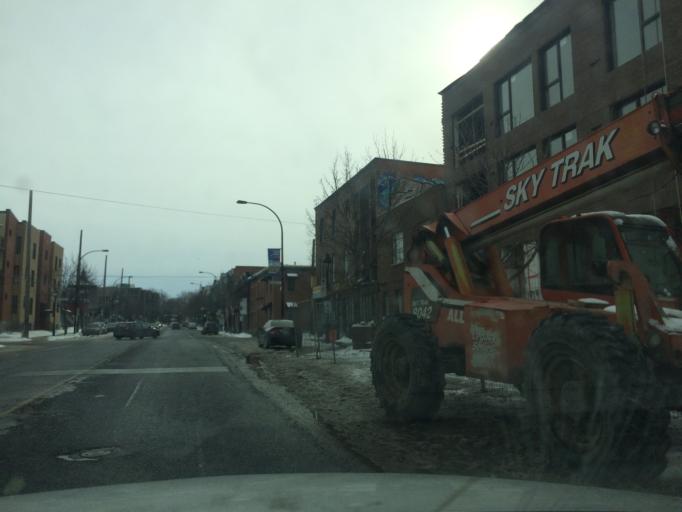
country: CA
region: Quebec
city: Westmount
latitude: 45.4805
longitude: -73.5586
